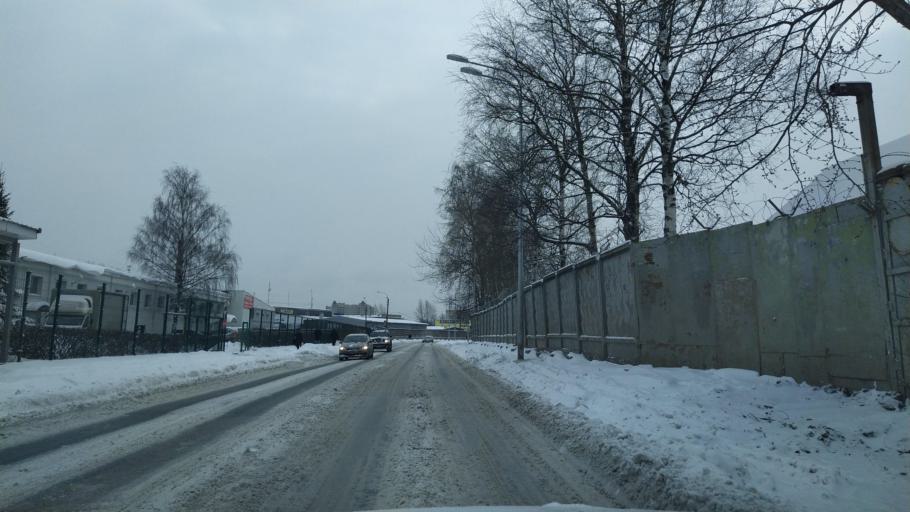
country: RU
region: St.-Petersburg
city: Novaya Derevnya
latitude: 59.9924
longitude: 30.2767
